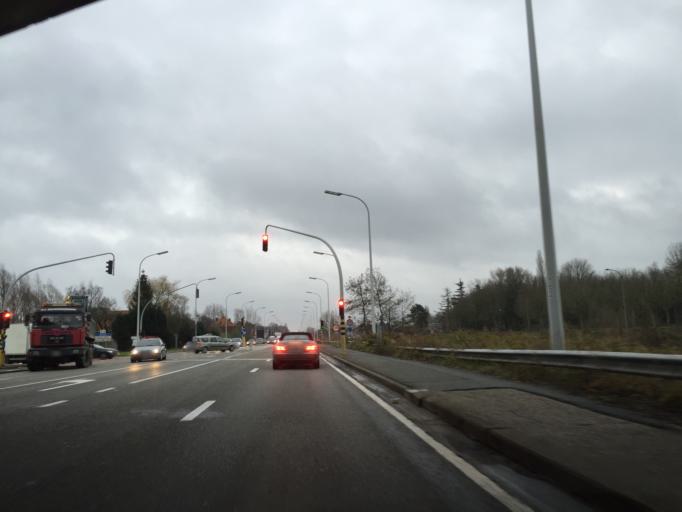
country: BE
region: Flanders
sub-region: Provincie Oost-Vlaanderen
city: Evergem
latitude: 51.0846
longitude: 3.6650
